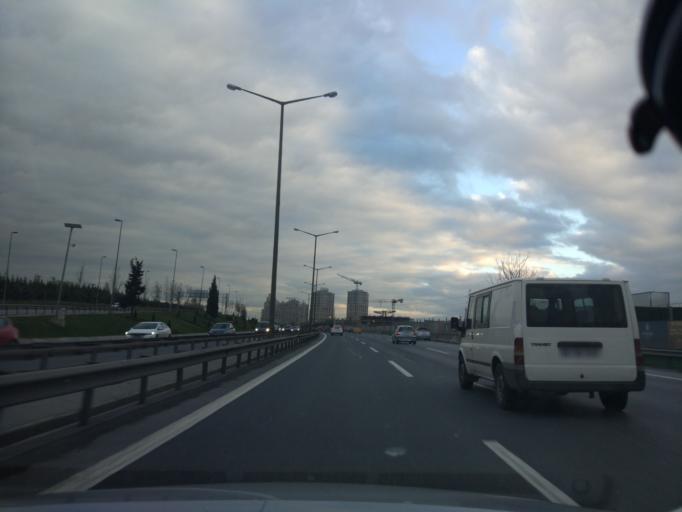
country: TR
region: Istanbul
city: Esenler
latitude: 41.0711
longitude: 28.8660
